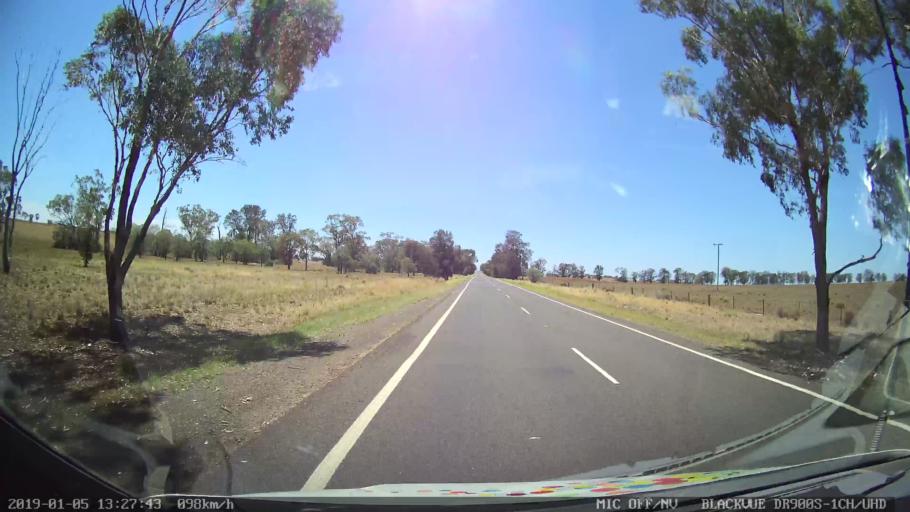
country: AU
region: New South Wales
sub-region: Gunnedah
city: Gunnedah
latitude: -31.0421
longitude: 150.0332
